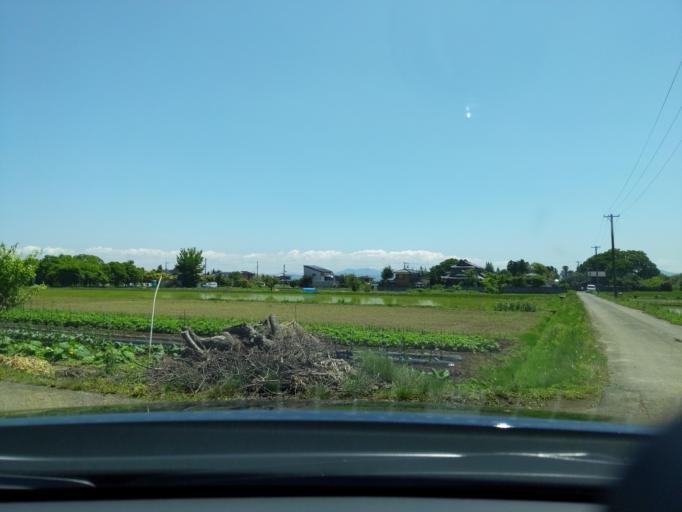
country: JP
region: Fukushima
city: Koriyama
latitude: 37.3874
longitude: 140.2945
